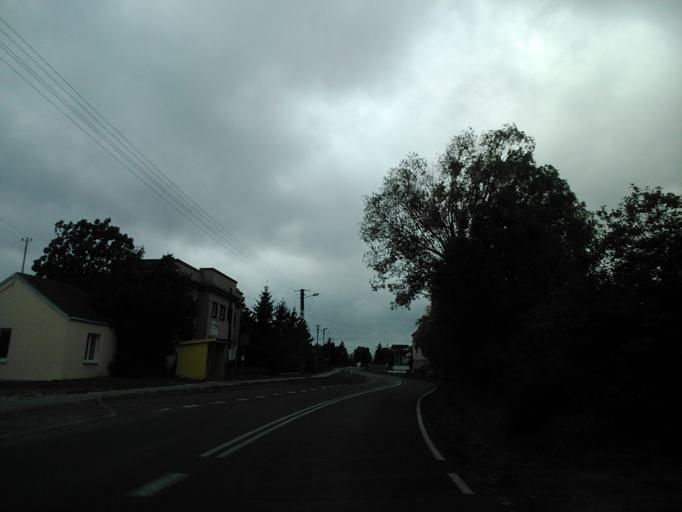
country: PL
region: Kujawsko-Pomorskie
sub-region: Powiat inowroclawski
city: Kruszwica
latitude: 52.6819
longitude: 18.2726
